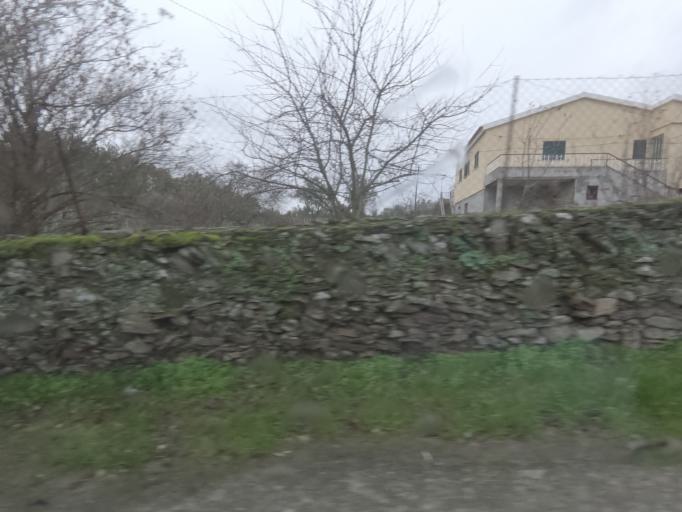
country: PT
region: Viseu
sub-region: Armamar
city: Armamar
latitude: 41.1643
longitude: -7.7135
